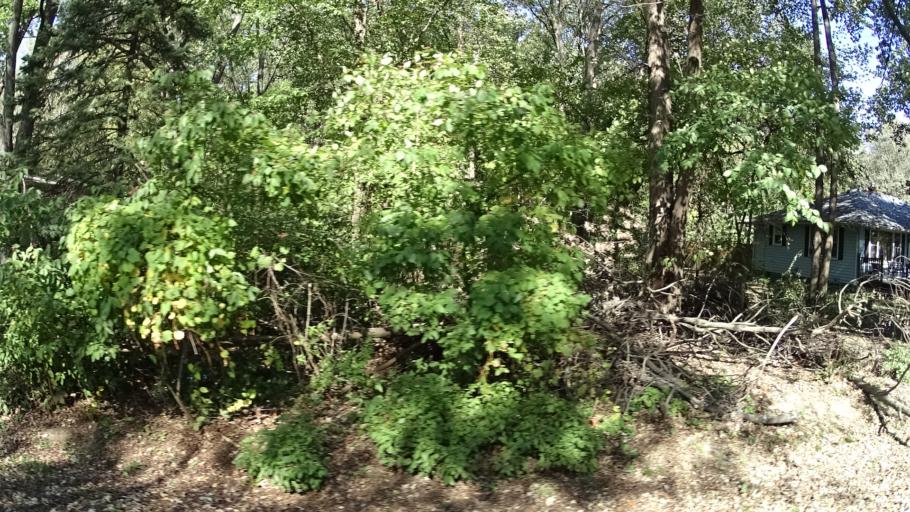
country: US
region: Ohio
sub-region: Lorain County
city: Vermilion
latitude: 41.4159
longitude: -82.3446
